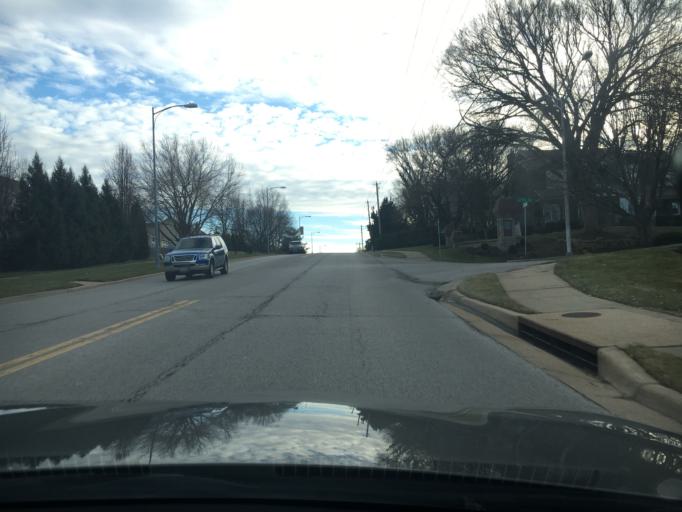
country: US
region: Kansas
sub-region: Johnson County
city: Leawood
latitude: 38.9011
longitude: -94.6306
